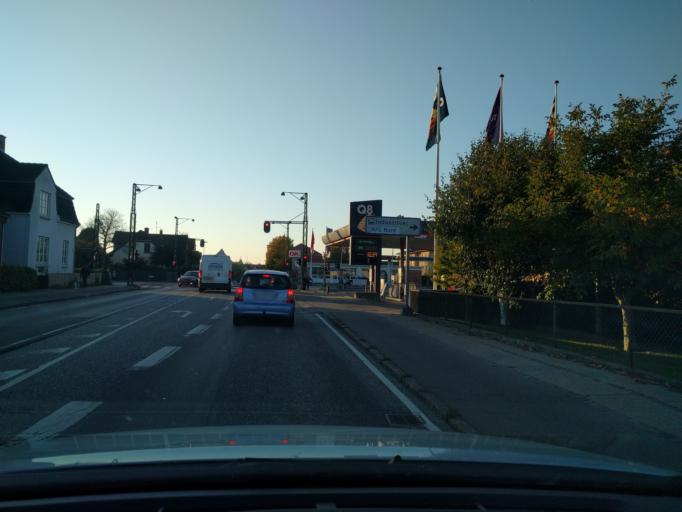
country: DK
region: Zealand
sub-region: Guldborgsund Kommune
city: Nykobing Falster
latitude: 54.7664
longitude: 11.8830
